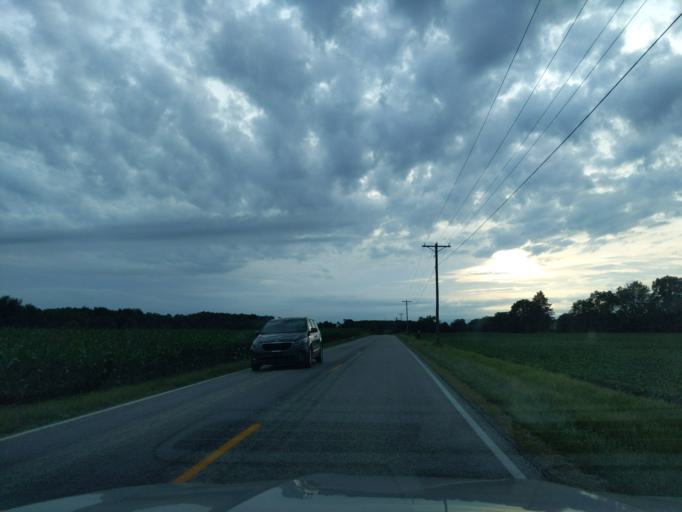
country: US
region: Indiana
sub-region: Ripley County
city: Osgood
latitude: 39.1978
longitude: -85.2927
